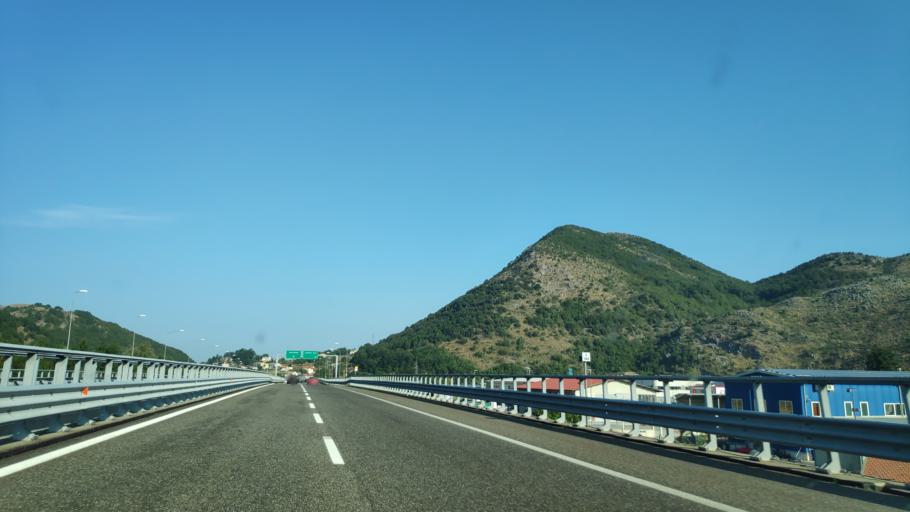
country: IT
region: Basilicate
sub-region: Provincia di Potenza
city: Lauria
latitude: 40.0154
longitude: 15.8946
